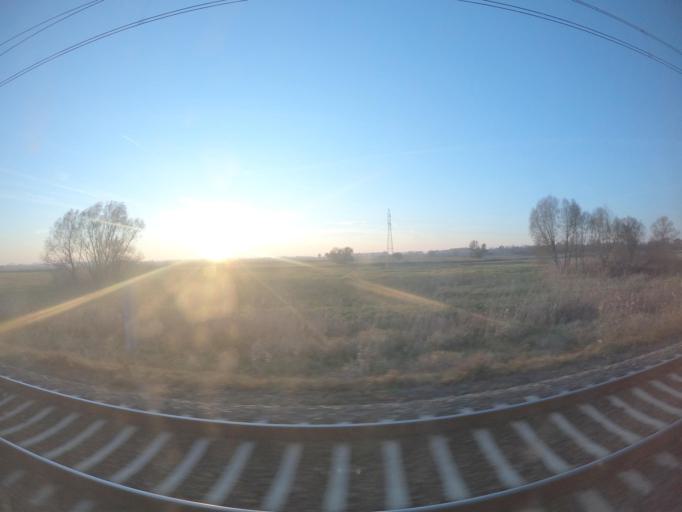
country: PL
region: Lubusz
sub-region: Powiat gorzowski
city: Kostrzyn nad Odra
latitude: 52.5614
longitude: 14.6482
